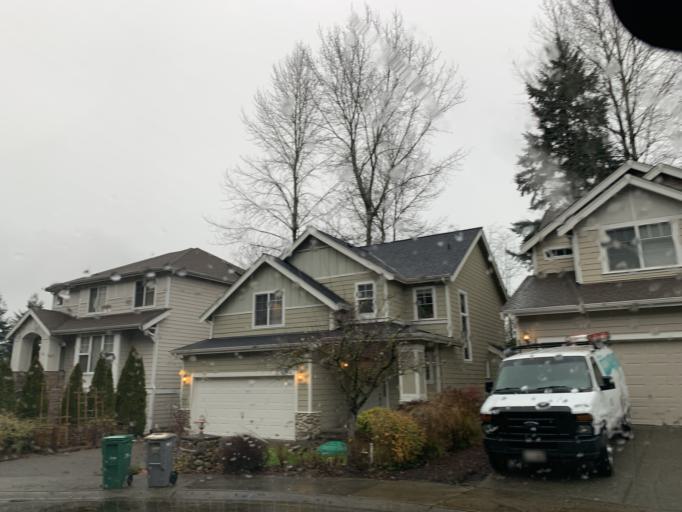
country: US
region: Washington
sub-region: King County
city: Woodinville
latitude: 47.7506
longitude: -122.1697
